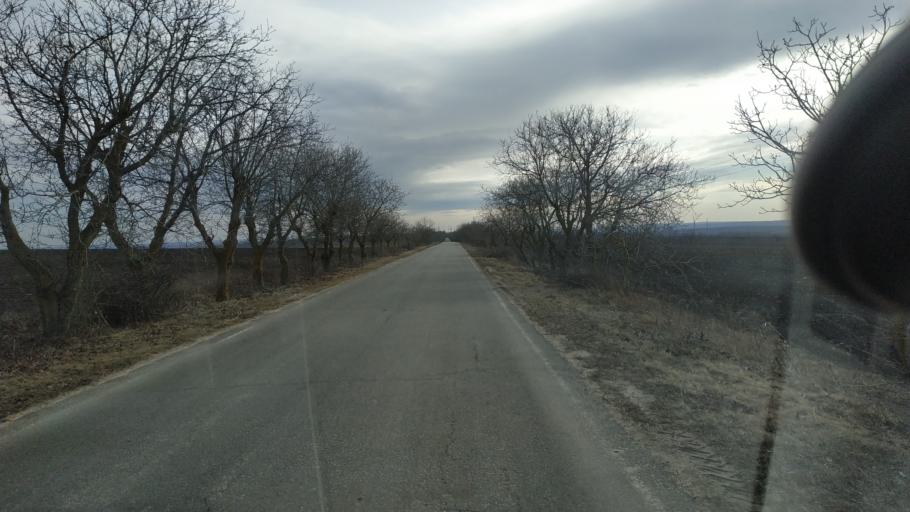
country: MD
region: Telenesti
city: Cocieri
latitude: 47.3509
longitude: 29.0468
